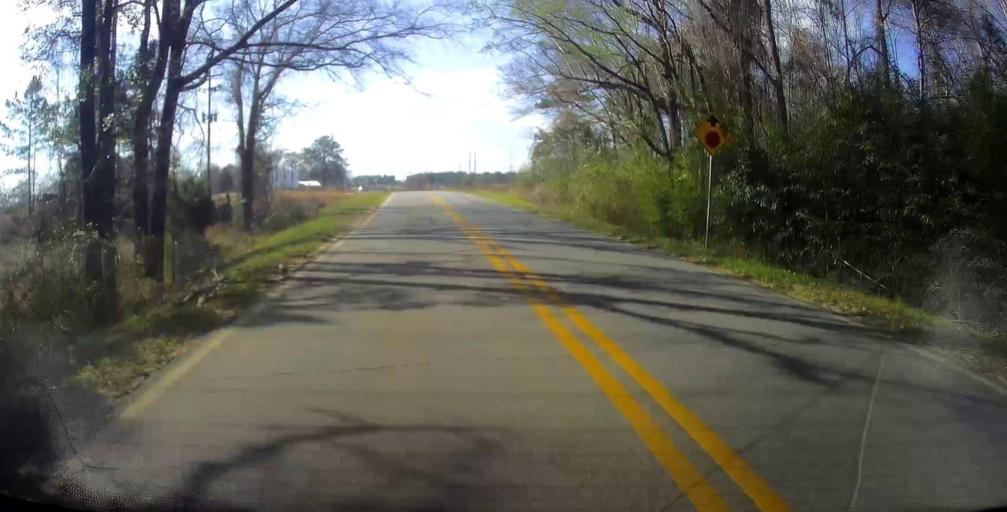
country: US
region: Georgia
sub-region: Laurens County
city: Dublin
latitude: 32.5679
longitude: -83.0309
